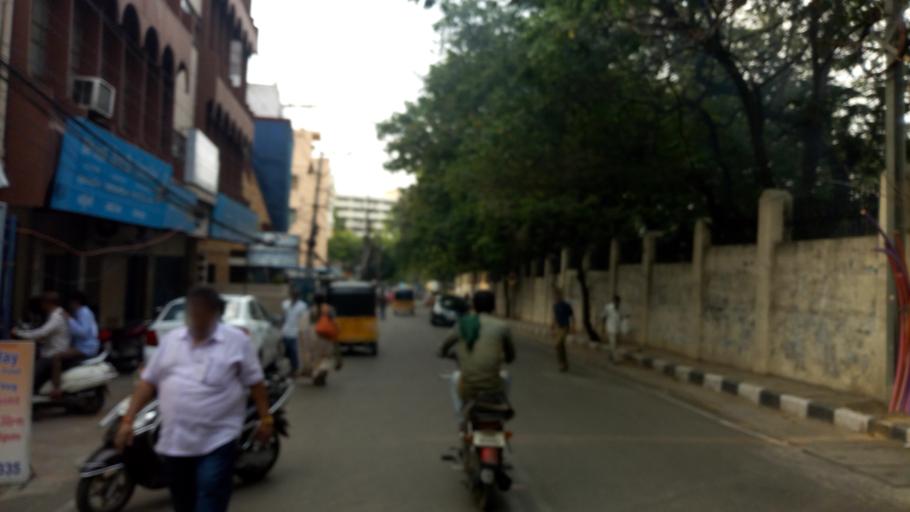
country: IN
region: Telangana
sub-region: Hyderabad
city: Hyderabad
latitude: 17.4053
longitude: 78.4727
